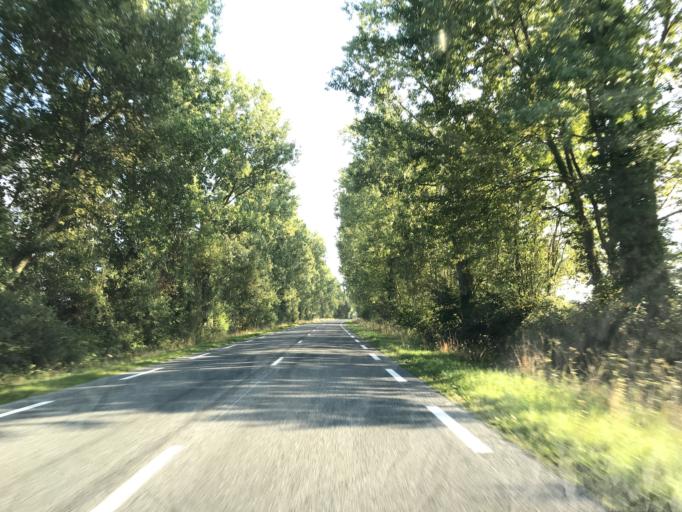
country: FR
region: Haute-Normandie
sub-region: Departement de la Seine-Maritime
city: La Remuee
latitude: 49.5250
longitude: 0.4204
